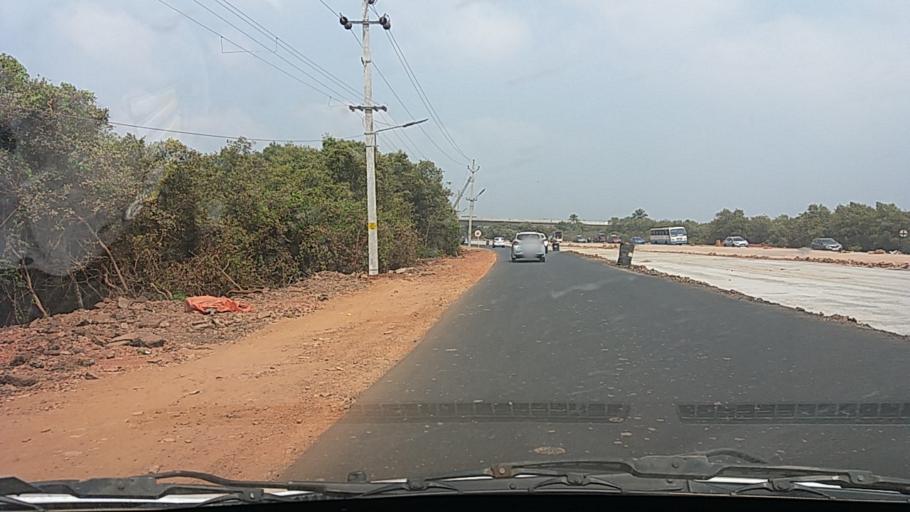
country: IN
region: Goa
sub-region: North Goa
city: Panaji
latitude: 15.4883
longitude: 73.8456
